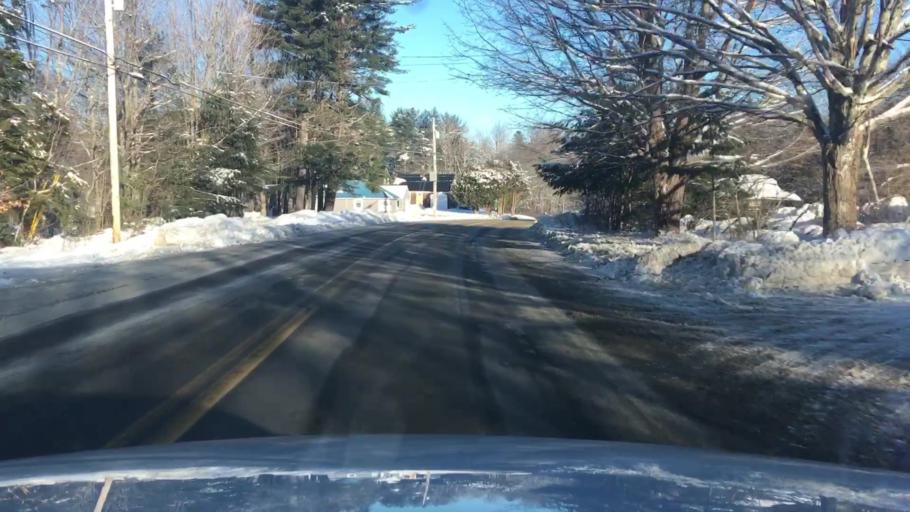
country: US
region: Maine
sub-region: Kennebec County
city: Readfield
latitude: 44.4395
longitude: -69.9682
